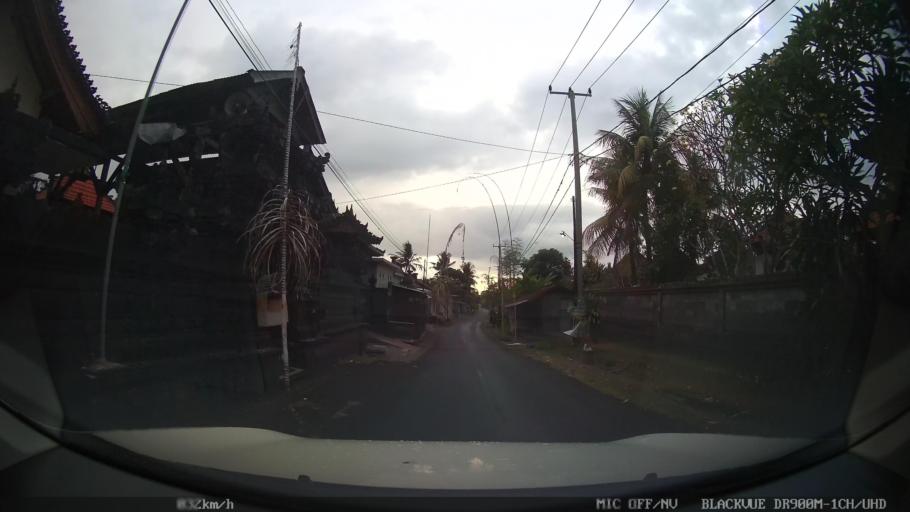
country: ID
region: Bali
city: Banjar Pasekan
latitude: -8.6257
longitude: 115.2798
